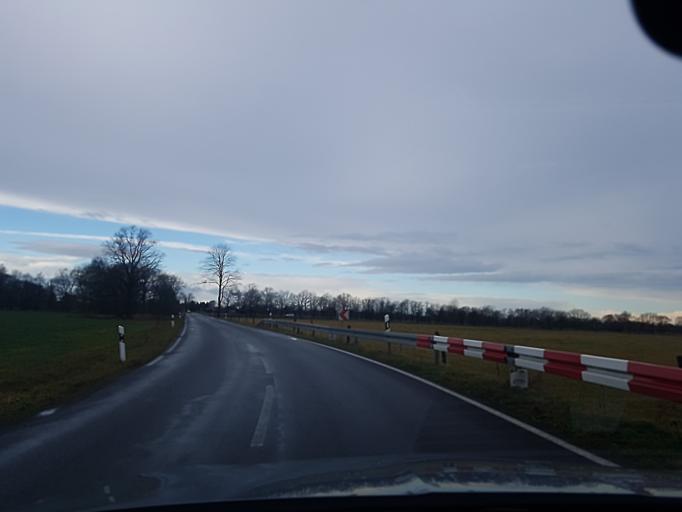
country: DE
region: Brandenburg
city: Schilda
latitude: 51.6073
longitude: 13.3226
